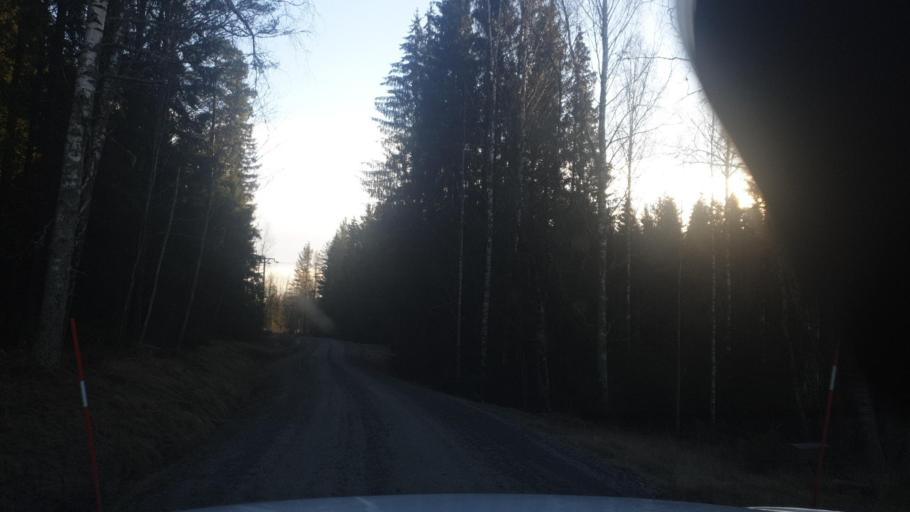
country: SE
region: Vaermland
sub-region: Sunne Kommun
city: Sunne
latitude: 59.6647
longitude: 13.0412
